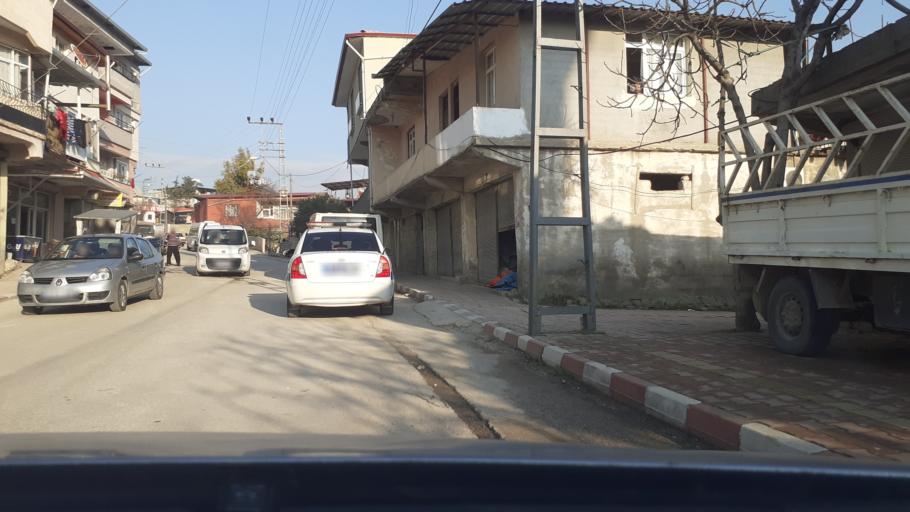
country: TR
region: Hatay
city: Fatikli
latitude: 36.1133
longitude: 36.2624
